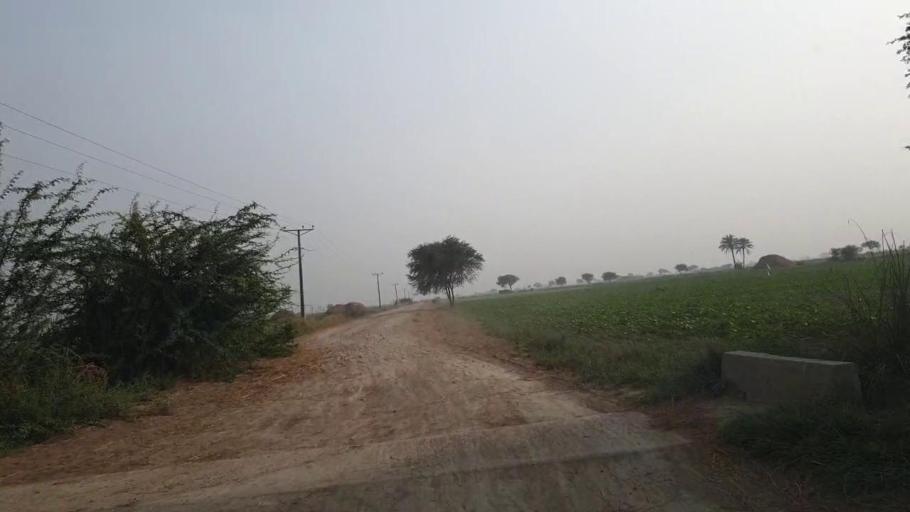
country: PK
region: Sindh
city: Mirpur Batoro
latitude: 24.5648
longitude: 68.4187
